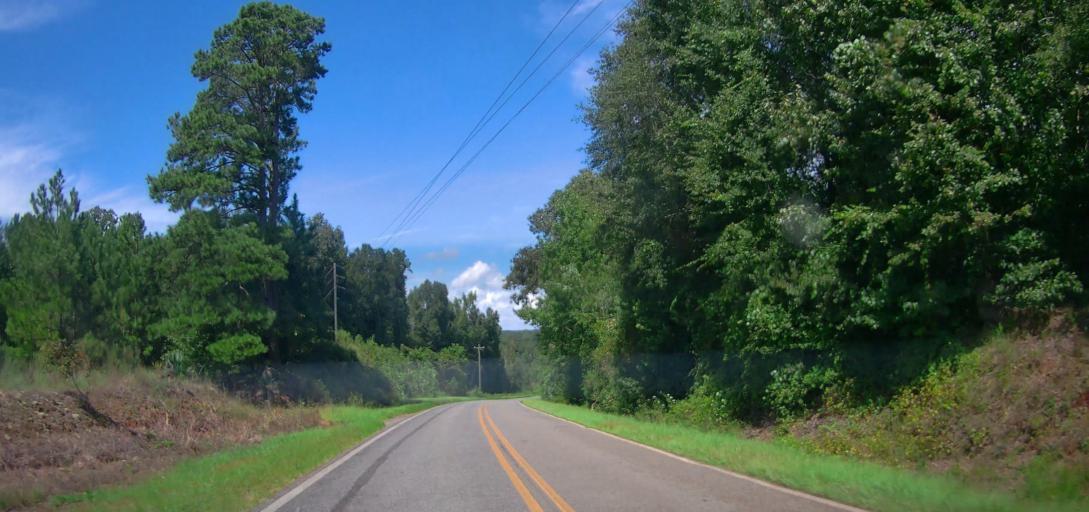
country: US
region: Georgia
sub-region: Macon County
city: Marshallville
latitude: 32.4746
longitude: -83.8670
